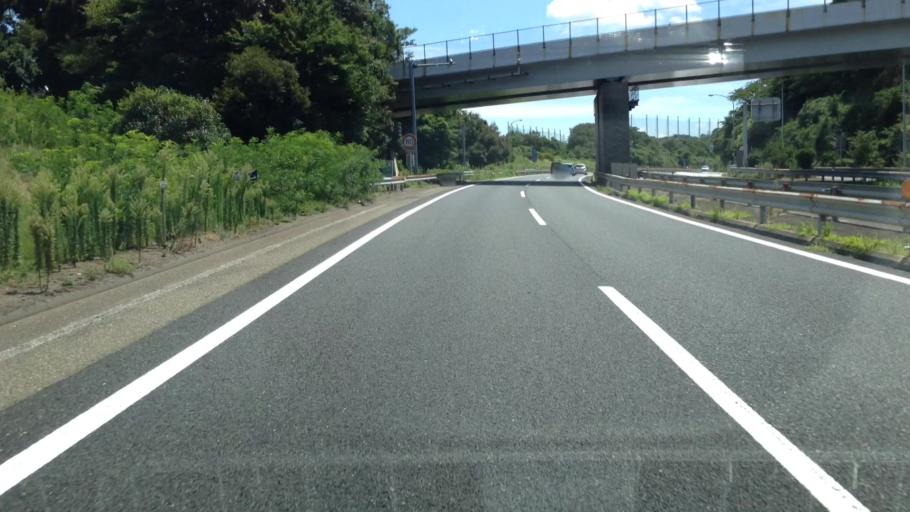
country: JP
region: Kanagawa
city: Yokosuka
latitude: 35.2775
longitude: 139.6337
